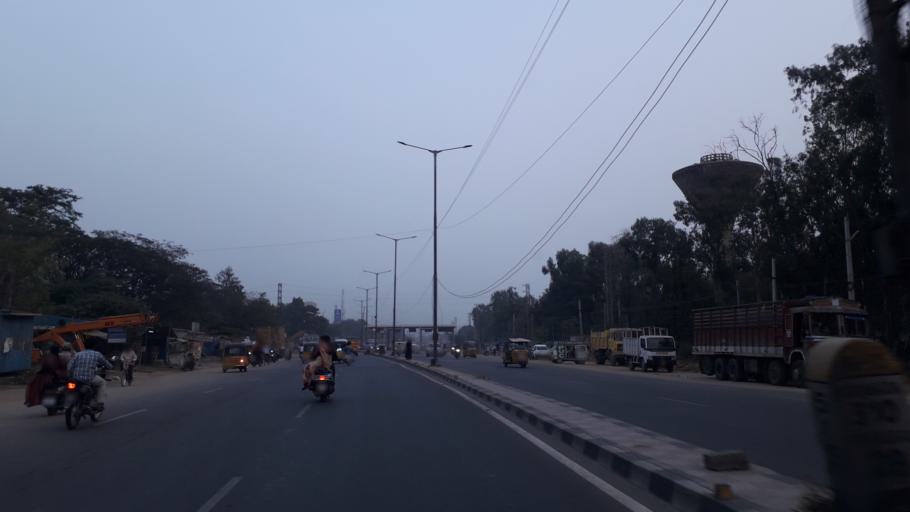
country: IN
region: Telangana
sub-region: Medak
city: Patancheru
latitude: 17.5249
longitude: 78.2717
